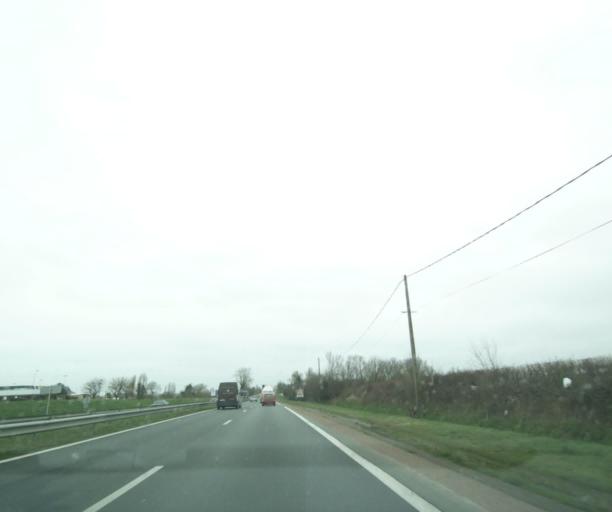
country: FR
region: Poitou-Charentes
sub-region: Departement de la Charente-Maritime
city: Angoulins
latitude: 46.1112
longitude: -1.1014
